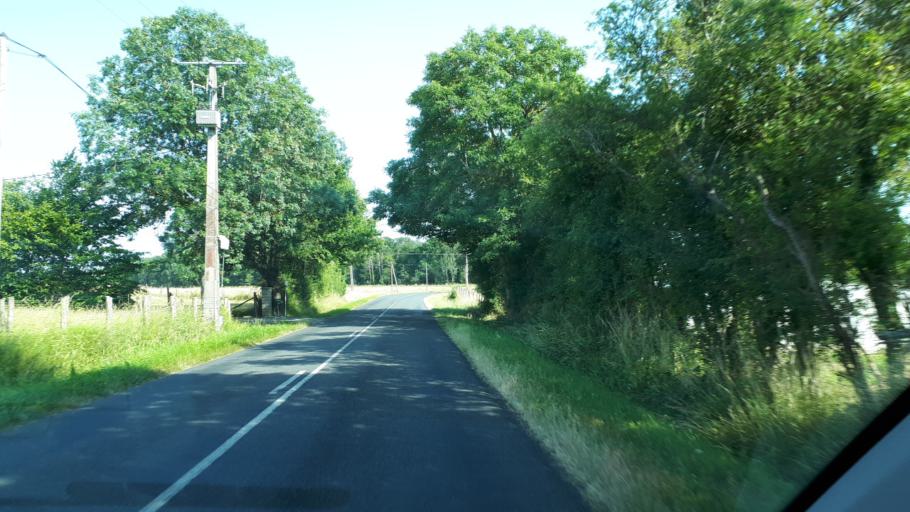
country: FR
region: Centre
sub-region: Departement du Loir-et-Cher
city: Droue
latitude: 47.9836
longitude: 1.0410
